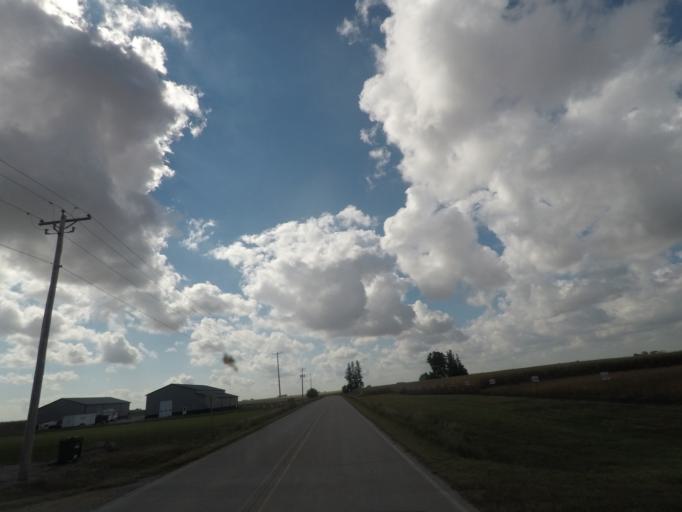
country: US
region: Iowa
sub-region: Story County
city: Nevada
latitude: 42.0065
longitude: -93.3192
